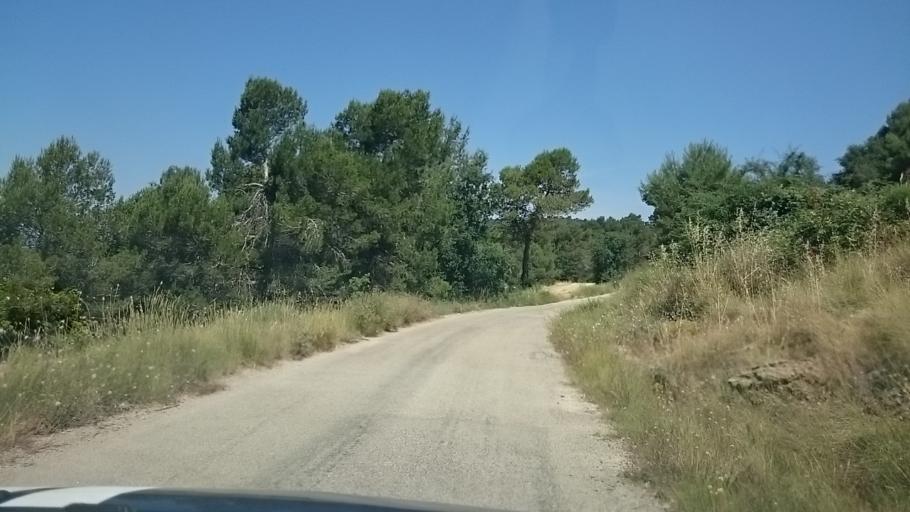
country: ES
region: Catalonia
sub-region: Provincia de Tarragona
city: Querol
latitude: 41.4029
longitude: 1.4177
